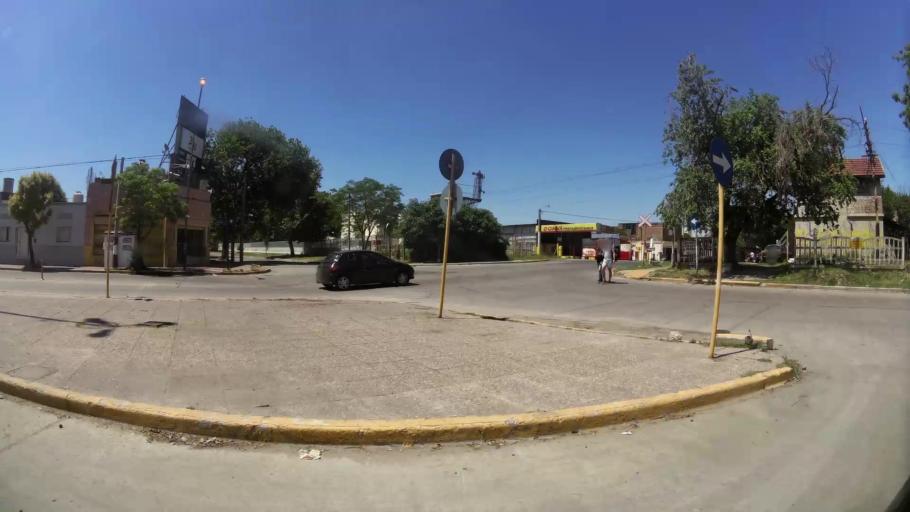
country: AR
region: Cordoba
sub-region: Departamento de Capital
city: Cordoba
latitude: -31.3871
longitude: -64.1921
